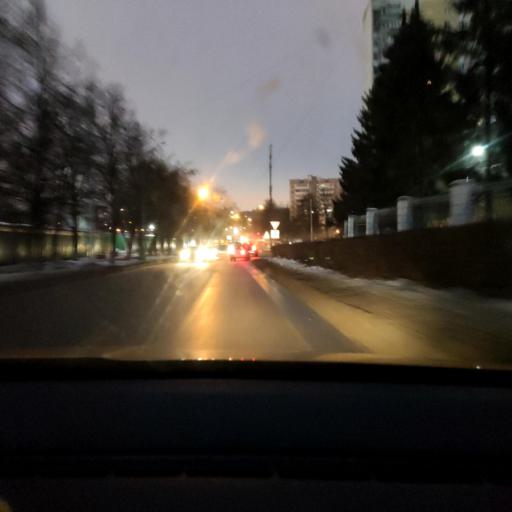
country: RU
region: Moskovskaya
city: Mosrentgen
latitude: 55.6154
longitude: 37.4695
